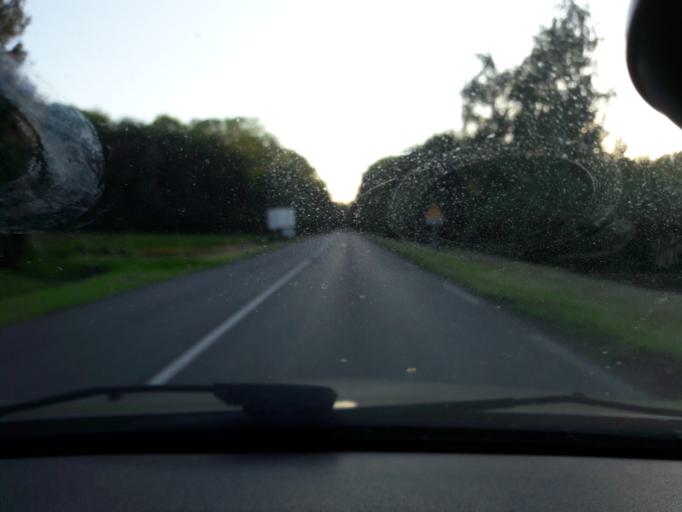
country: FR
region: Nord-Pas-de-Calais
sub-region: Departement du Nord
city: Recquignies
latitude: 50.2765
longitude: 4.0306
